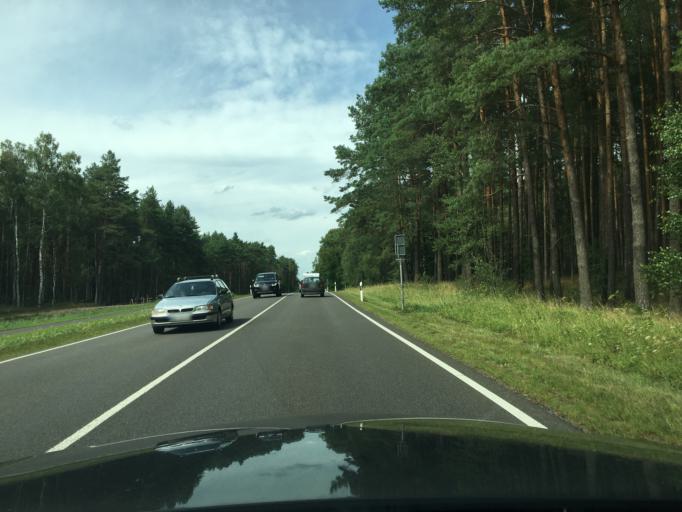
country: DE
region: Mecklenburg-Vorpommern
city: Neustrelitz
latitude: 53.2944
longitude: 13.1074
